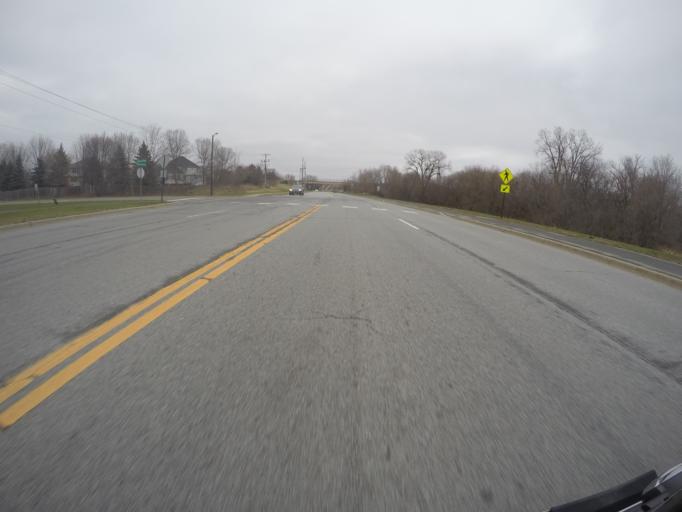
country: US
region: Minnesota
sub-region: Hennepin County
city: Eden Prairie
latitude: 44.8691
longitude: -93.4695
